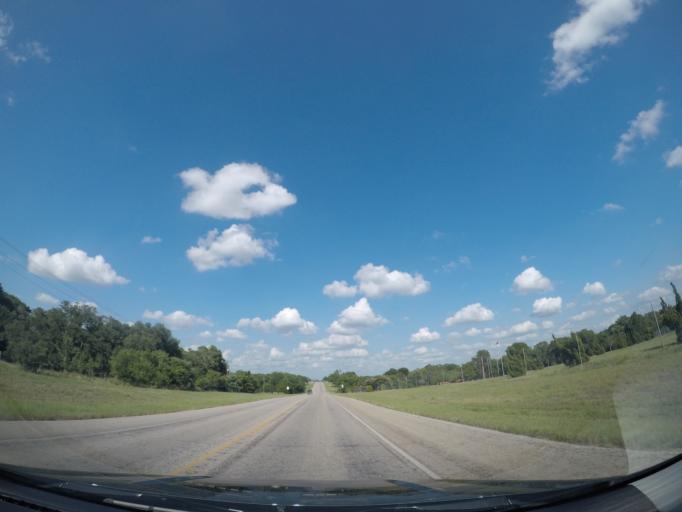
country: US
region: Texas
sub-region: Lavaca County
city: Shiner
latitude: 29.4285
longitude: -97.0661
